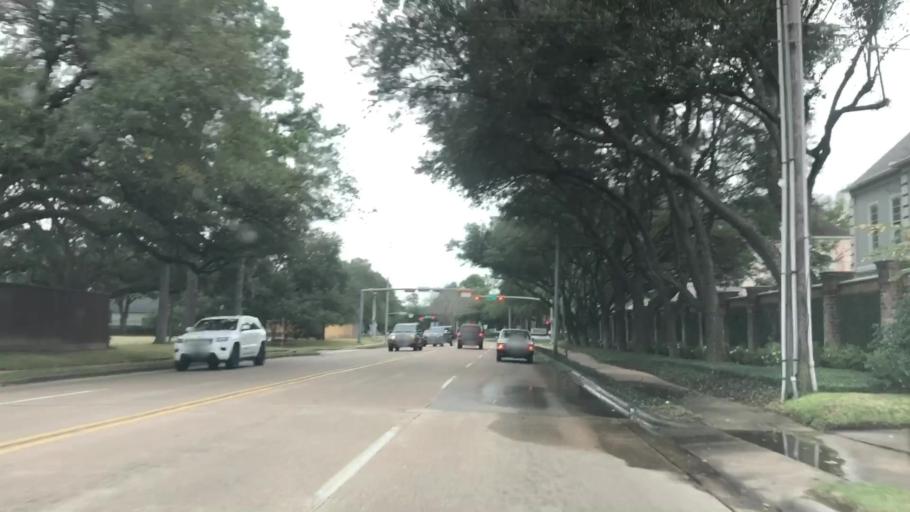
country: US
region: Texas
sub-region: Harris County
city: Hunters Creek Village
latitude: 29.7660
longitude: -95.4783
